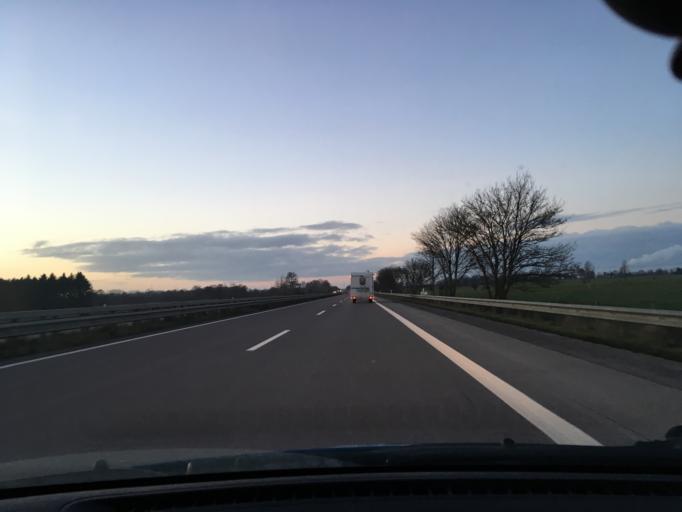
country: DE
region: Schleswig-Holstein
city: Hohenfelde
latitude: 53.8327
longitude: 9.6248
